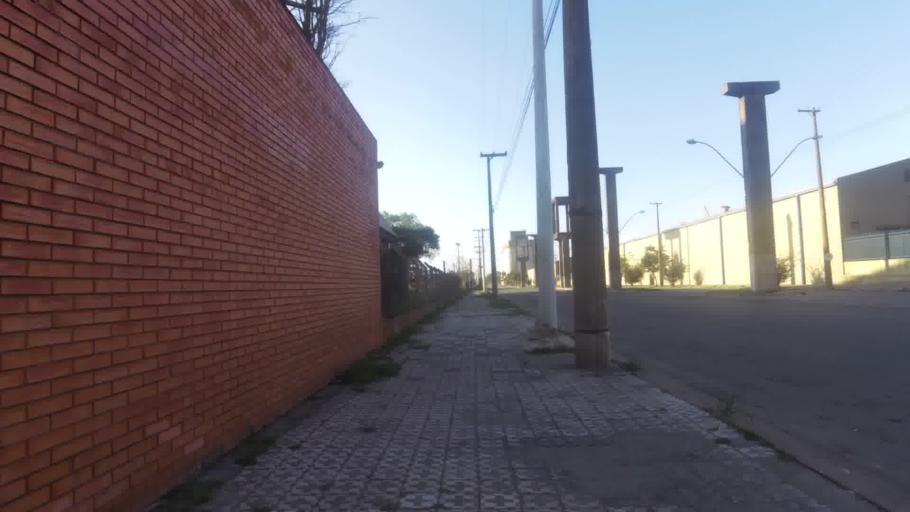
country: BR
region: Rio Grande do Sul
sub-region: Rio Grande
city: Rio Grande
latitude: -32.0399
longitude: -52.0775
